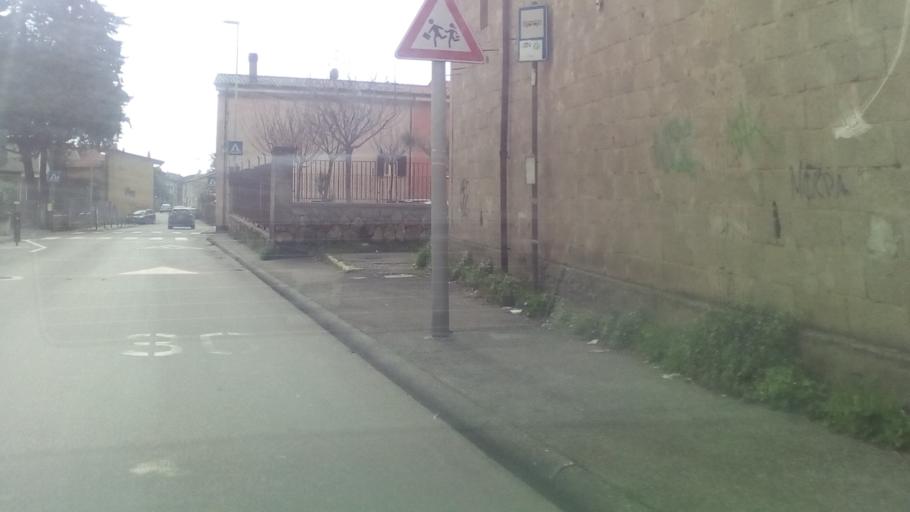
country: IT
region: Tuscany
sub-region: Provincia di Massa-Carrara
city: Carrara
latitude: 44.0621
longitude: 10.0750
